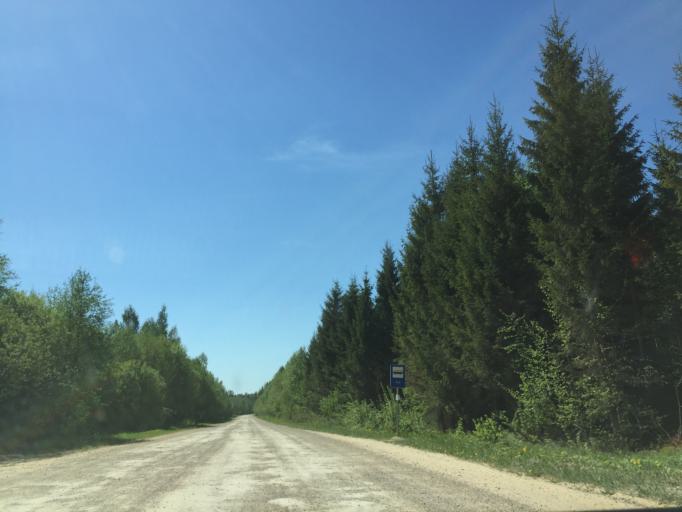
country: LV
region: Kegums
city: Kegums
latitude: 56.8738
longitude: 24.7773
